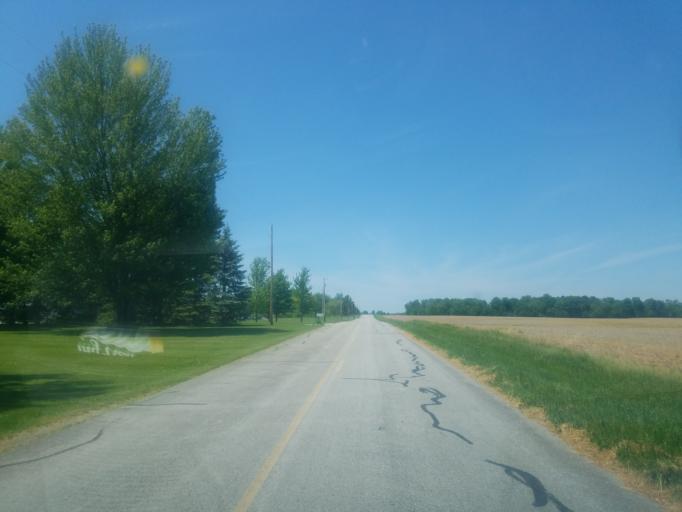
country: US
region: Ohio
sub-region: Huron County
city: New London
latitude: 41.1161
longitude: -82.3827
